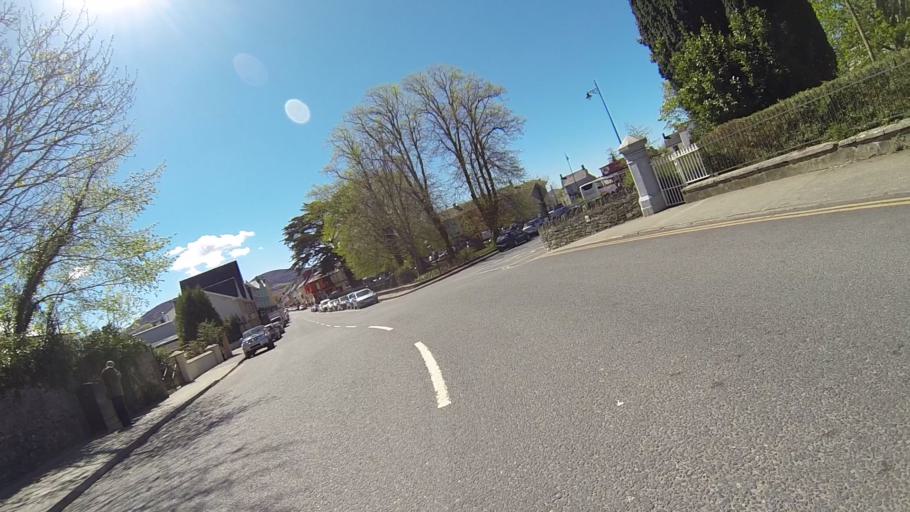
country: IE
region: Munster
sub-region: Ciarrai
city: Kenmare
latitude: 51.8811
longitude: -9.5833
